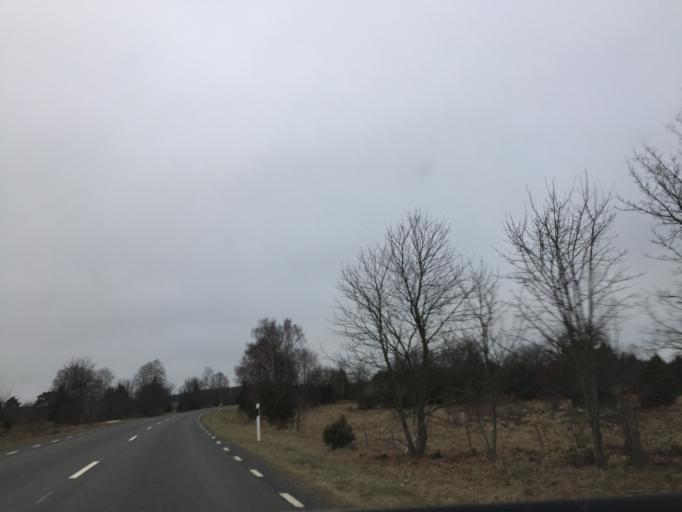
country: EE
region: Saare
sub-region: Kuressaare linn
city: Kuressaare
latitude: 58.5388
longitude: 22.3381
